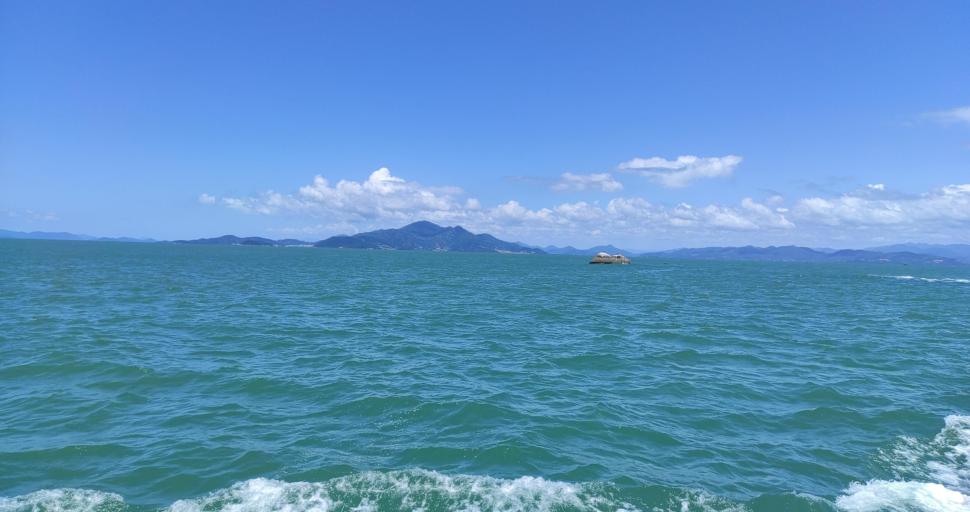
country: BR
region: Santa Catarina
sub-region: Porto Belo
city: Porto Belo
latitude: -27.2221
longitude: -48.5115
